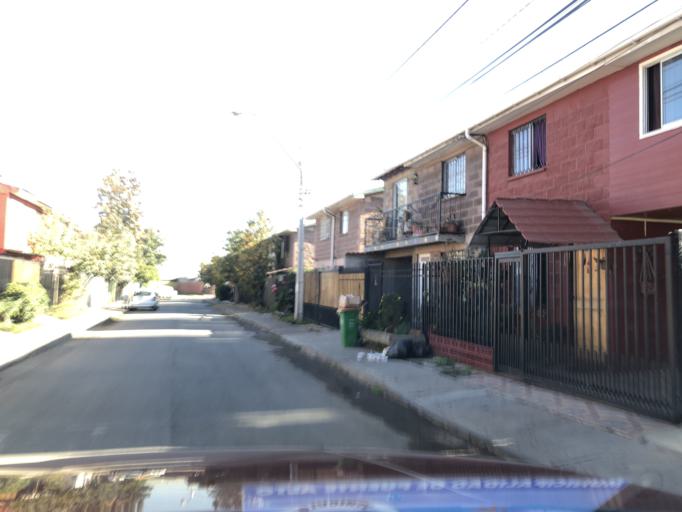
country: CL
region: Santiago Metropolitan
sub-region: Provincia de Cordillera
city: Puente Alto
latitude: -33.5940
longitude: -70.5567
